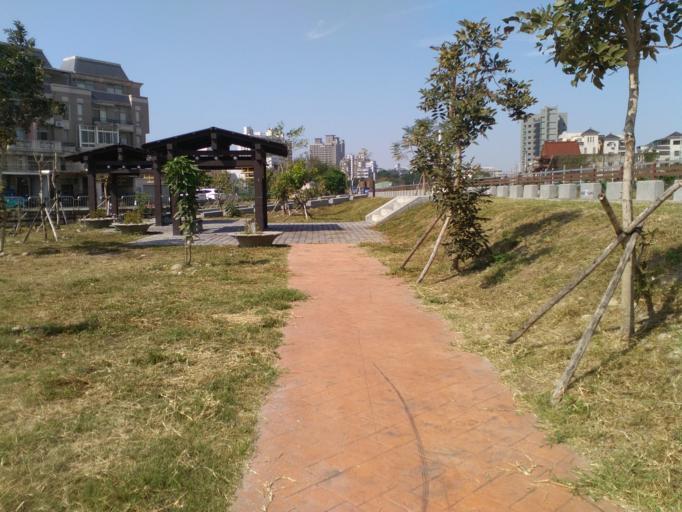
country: TW
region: Taiwan
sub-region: Taichung City
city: Taichung
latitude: 24.1111
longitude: 120.6723
